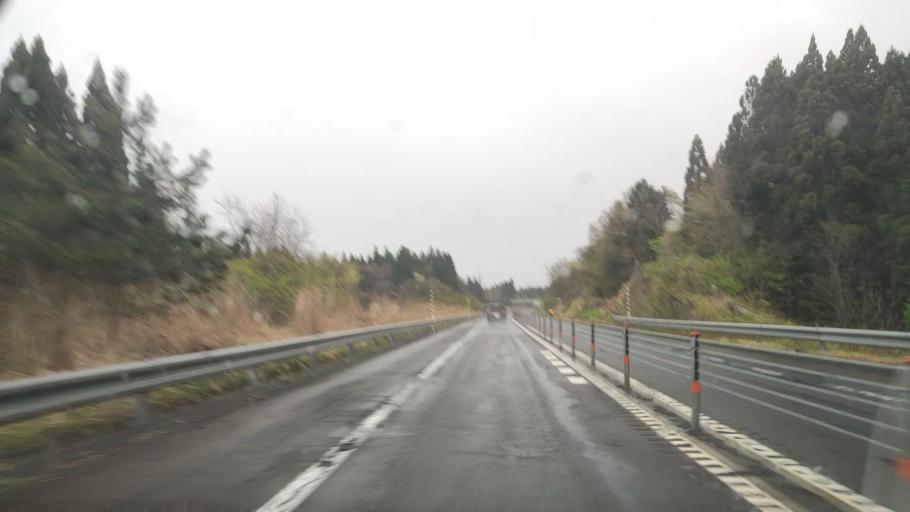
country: JP
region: Akita
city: Noshiromachi
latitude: 40.1715
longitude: 140.0533
